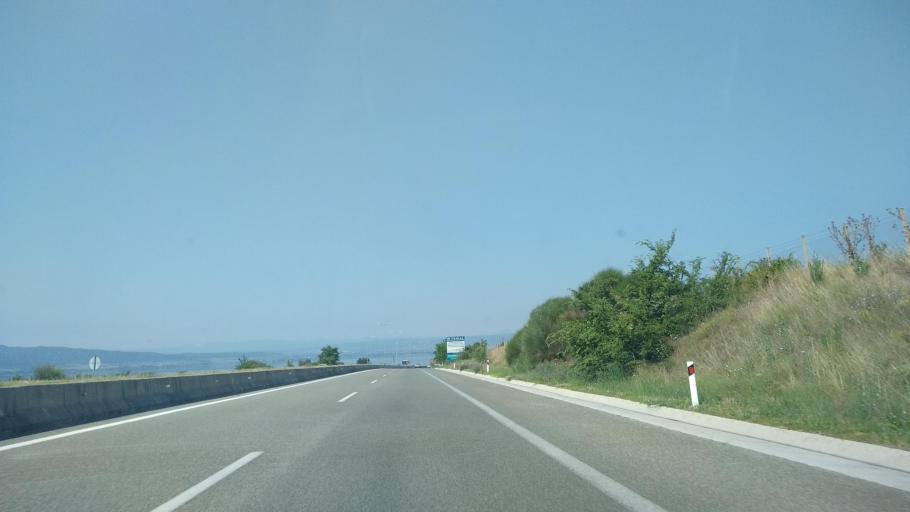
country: GR
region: Central Macedonia
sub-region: Nomos Thessalonikis
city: Stavros
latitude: 40.6768
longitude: 23.6048
